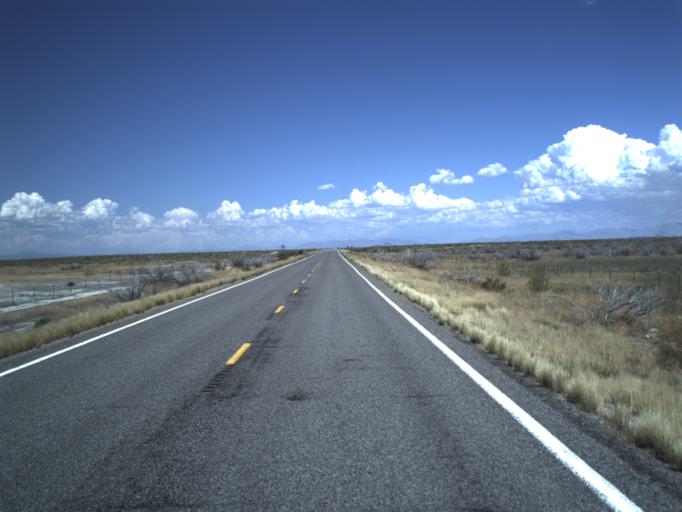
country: US
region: Utah
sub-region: Millard County
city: Delta
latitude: 39.2844
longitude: -112.8388
